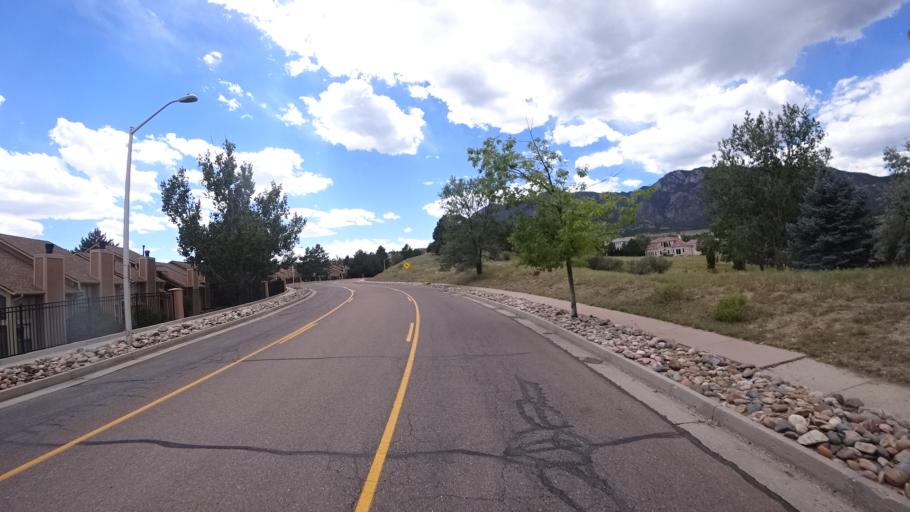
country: US
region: Colorado
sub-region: El Paso County
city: Stratmoor
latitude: 38.7744
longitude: -104.8215
